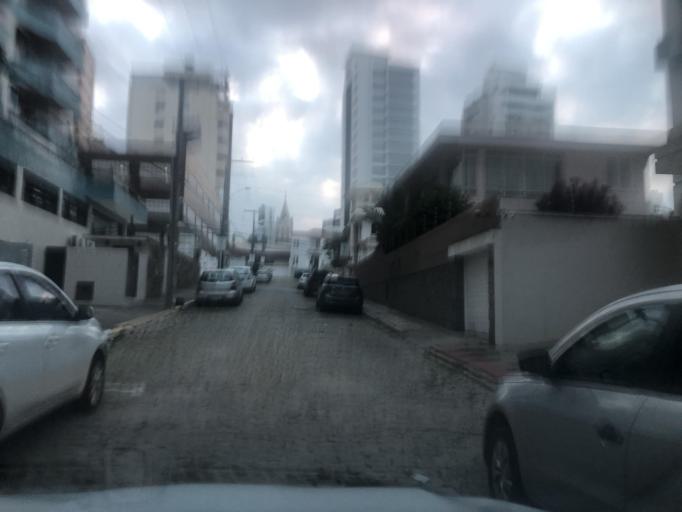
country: BR
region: Santa Catarina
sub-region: Florianopolis
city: Florianopolis
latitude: -27.5945
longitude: -48.5485
